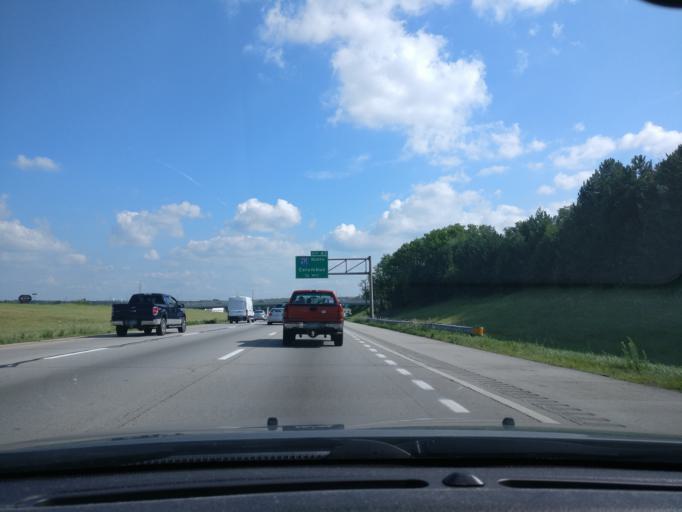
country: US
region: Ohio
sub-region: Montgomery County
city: West Carrollton City
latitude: 39.6324
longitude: -84.2309
